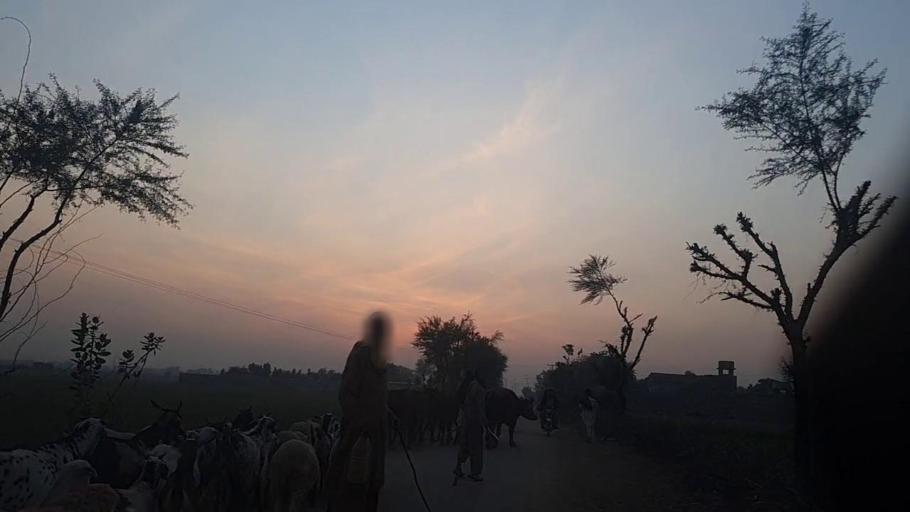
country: PK
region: Sindh
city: Sakrand
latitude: 26.1014
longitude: 68.3165
